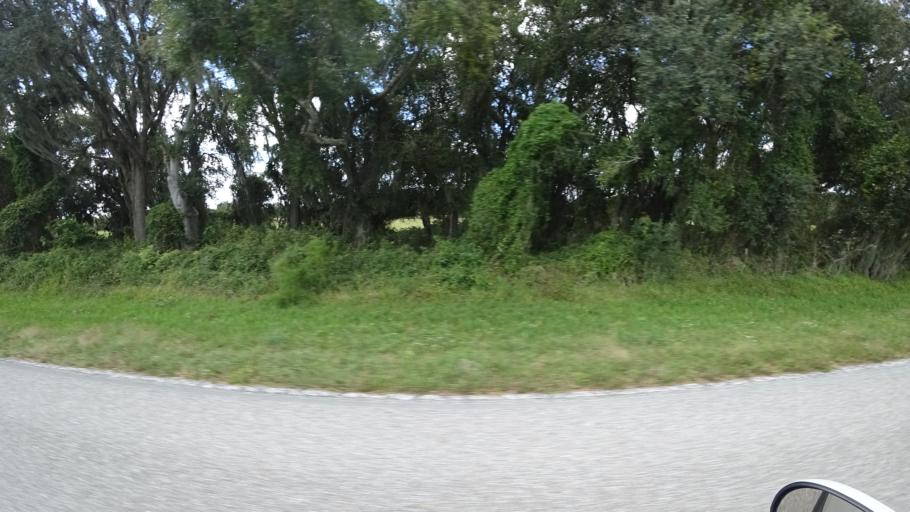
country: US
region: Florida
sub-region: Sarasota County
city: Lake Sarasota
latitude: 27.3270
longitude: -82.1667
